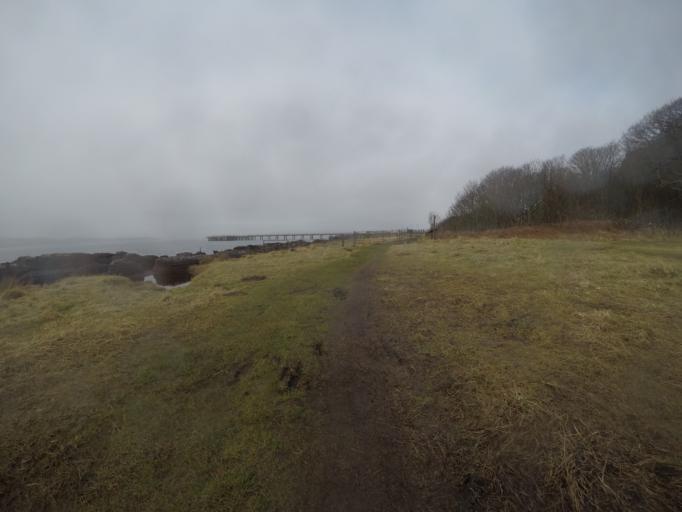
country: GB
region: Scotland
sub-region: North Ayrshire
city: Millport
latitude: 55.7126
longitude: -4.9033
